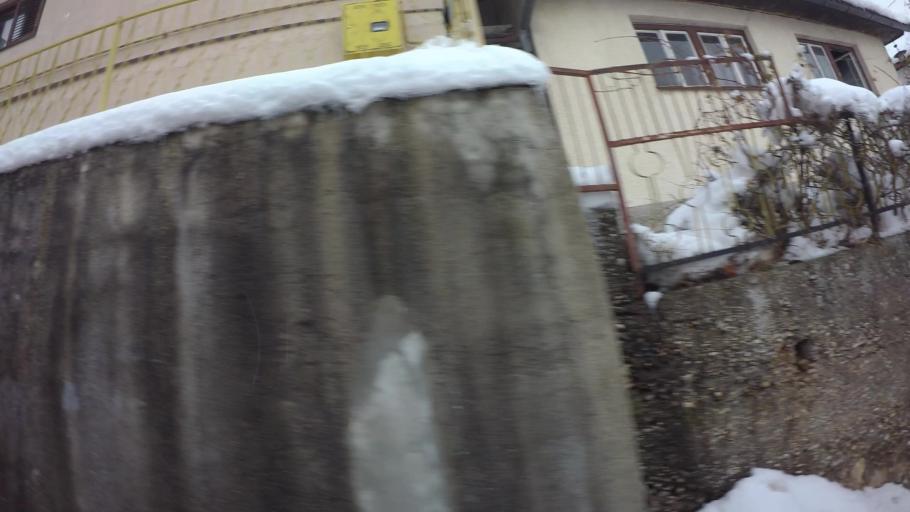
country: BA
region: Federation of Bosnia and Herzegovina
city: Kobilja Glava
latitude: 43.8675
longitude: 18.4374
